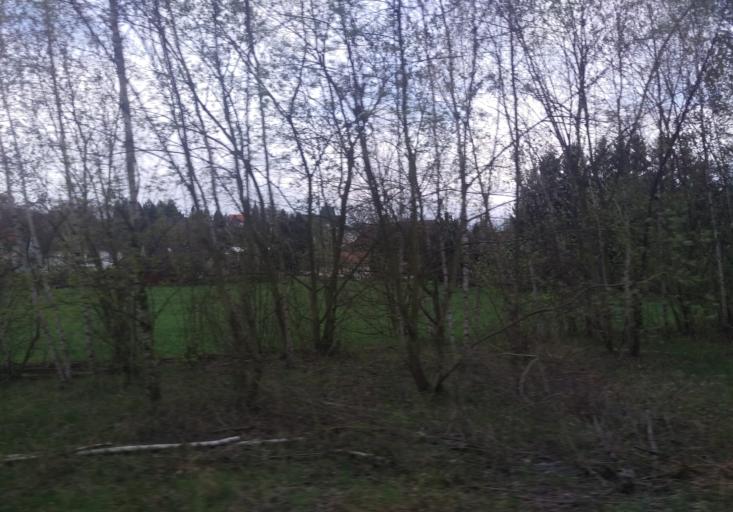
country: DE
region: Lower Saxony
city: Vienenburg
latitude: 51.9548
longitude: 10.5704
